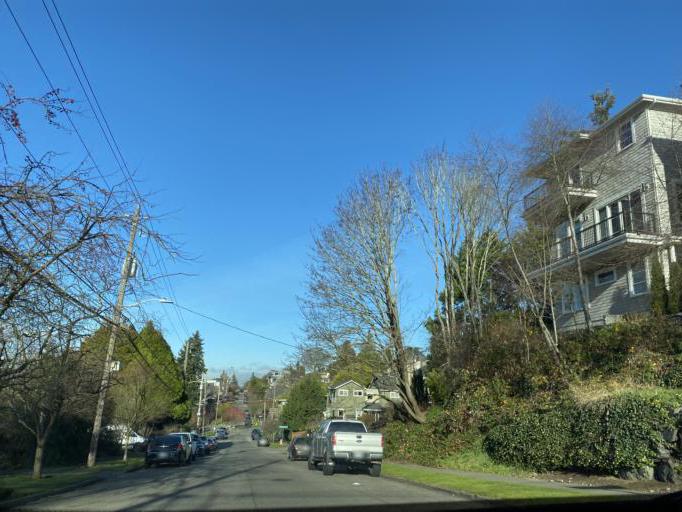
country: US
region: Washington
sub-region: King County
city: Seattle
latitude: 47.6436
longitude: -122.3715
